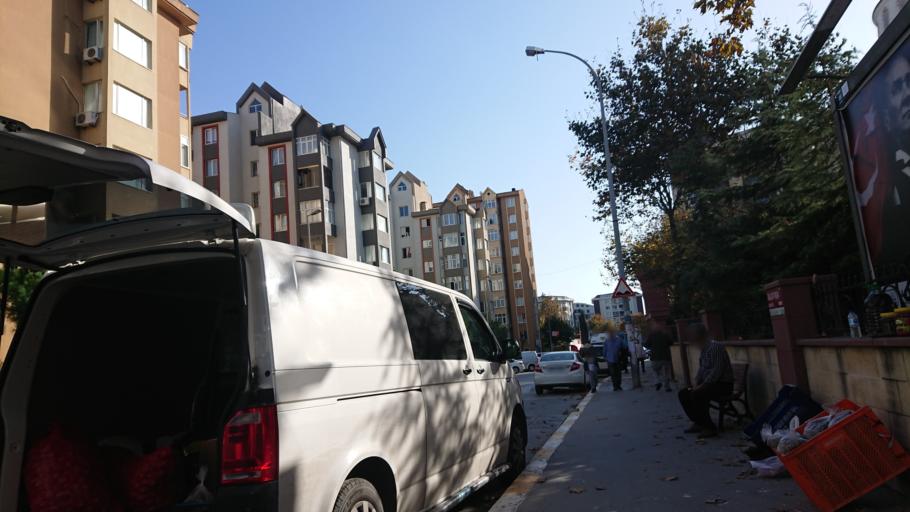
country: TR
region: Istanbul
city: Esenyurt
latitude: 41.0591
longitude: 28.6725
